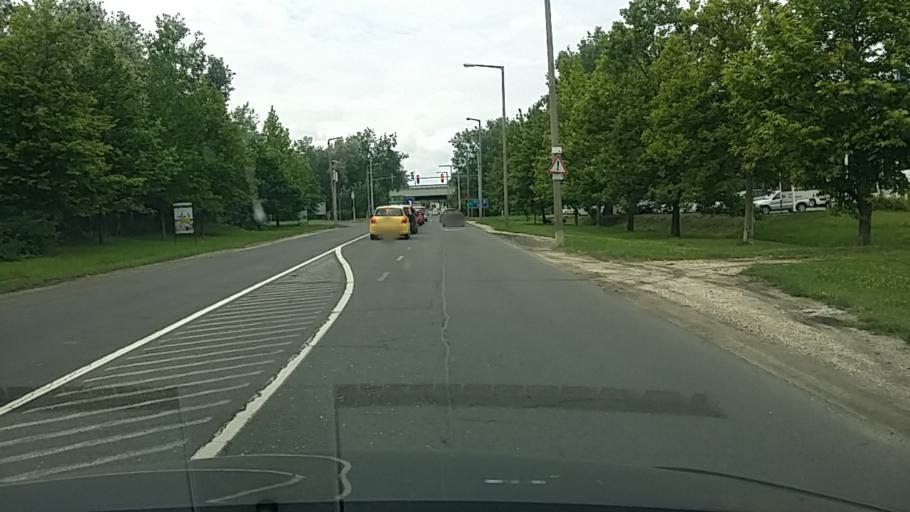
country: HU
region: Pest
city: Godollo
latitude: 47.6127
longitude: 19.3344
